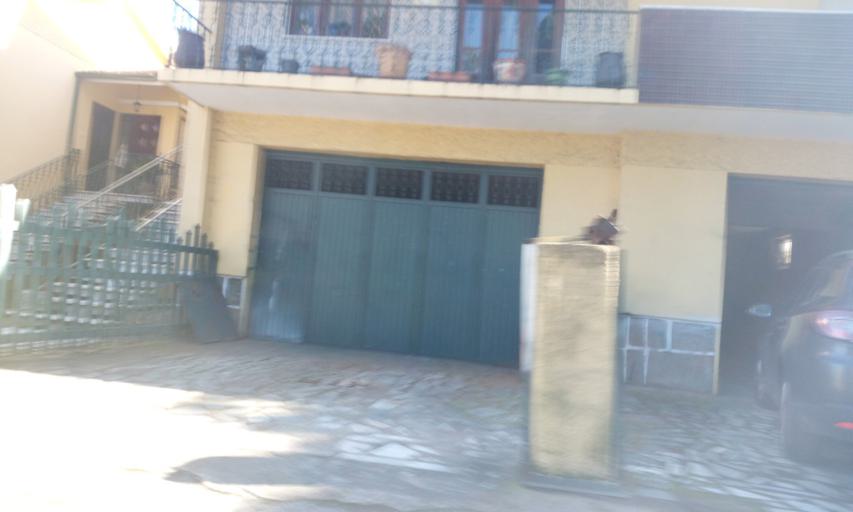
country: PT
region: Guarda
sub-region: Seia
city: Seia
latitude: 40.4738
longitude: -7.6243
